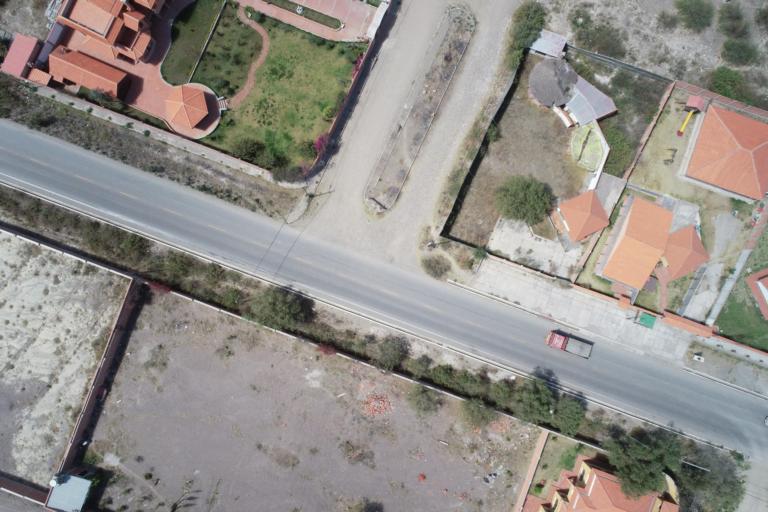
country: BO
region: La Paz
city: La Paz
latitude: -16.6494
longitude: -68.0374
